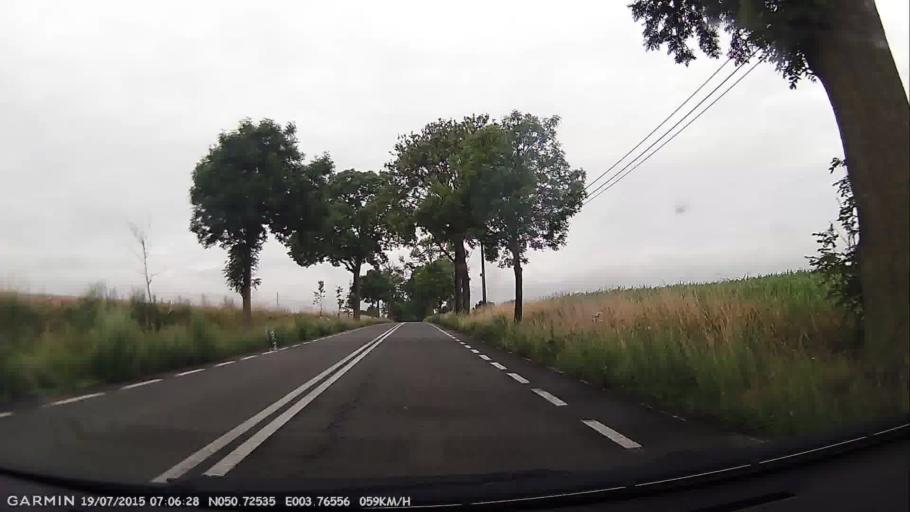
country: BE
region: Wallonia
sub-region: Province du Hainaut
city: Flobecq
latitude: 50.7254
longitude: 3.7654
